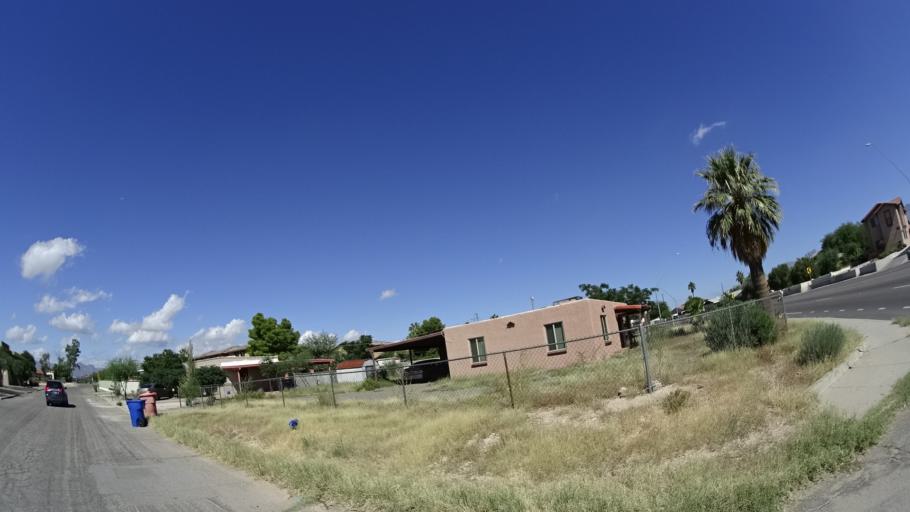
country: US
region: Arizona
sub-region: Pima County
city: Tucson
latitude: 32.2468
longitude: -110.9597
